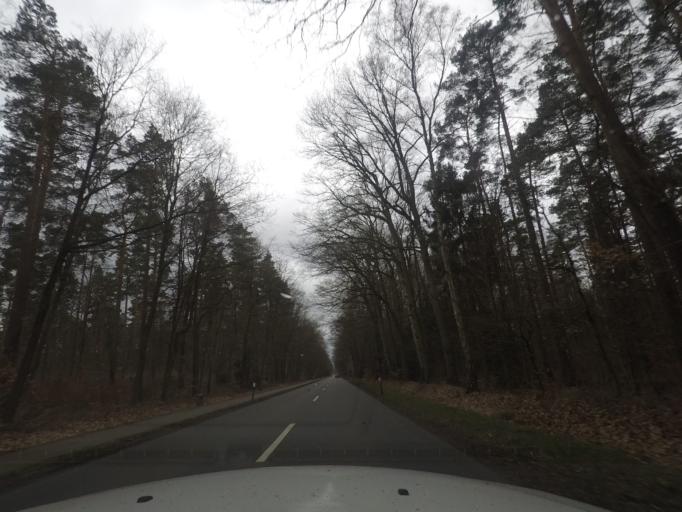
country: DE
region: Lower Saxony
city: Emmendorf
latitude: 52.9996
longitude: 10.5887
